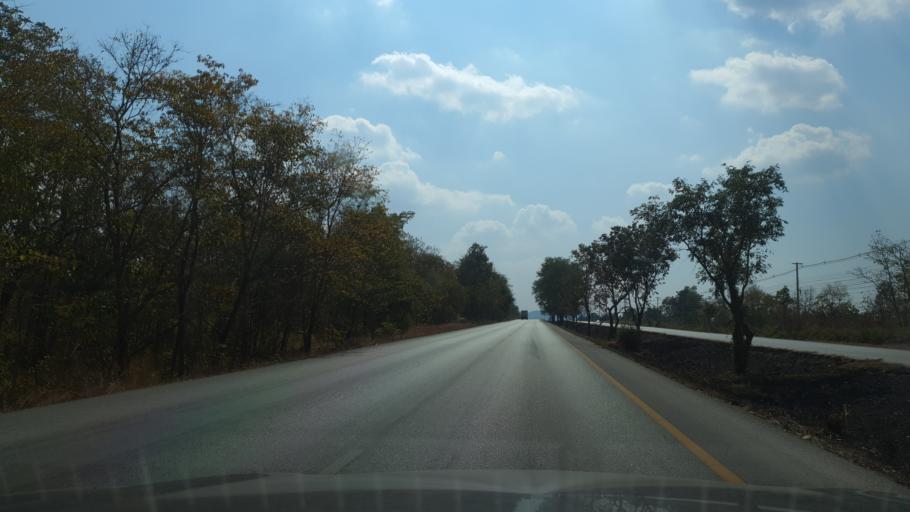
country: TH
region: Lampang
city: Mae Phrik
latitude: 17.3901
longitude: 99.1487
